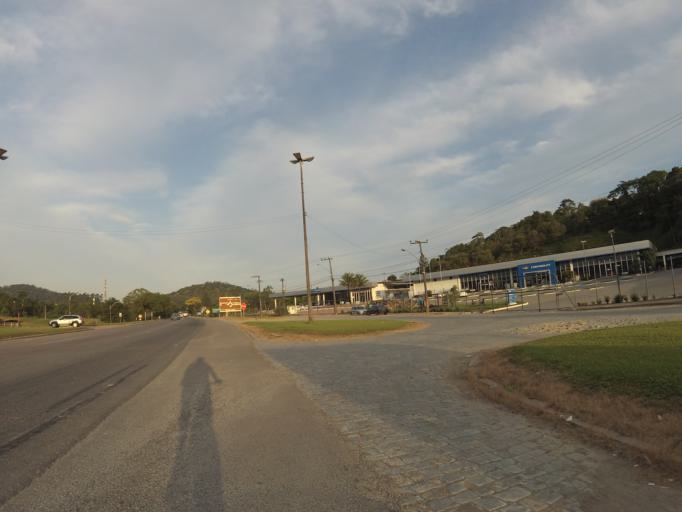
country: BR
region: Santa Catarina
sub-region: Indaial
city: Indaial
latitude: -26.8842
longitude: -49.1471
